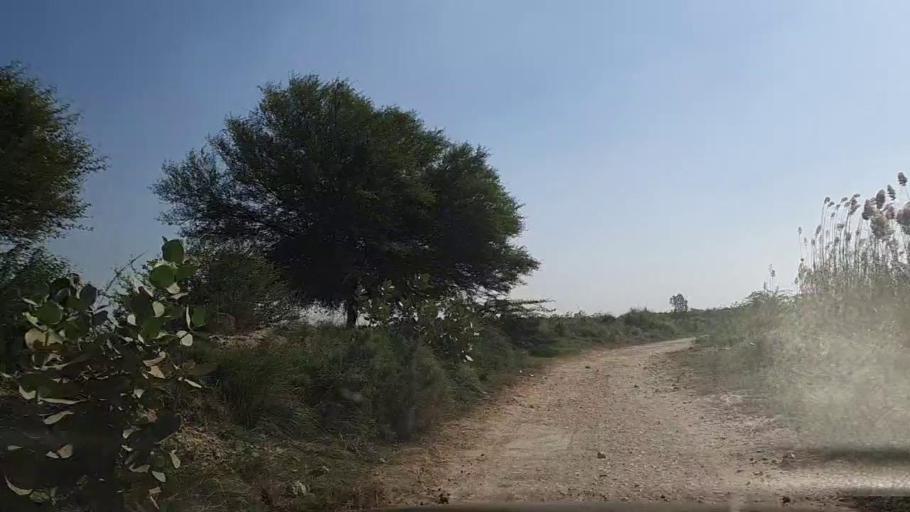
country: PK
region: Sindh
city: Daro Mehar
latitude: 24.8265
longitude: 68.0881
